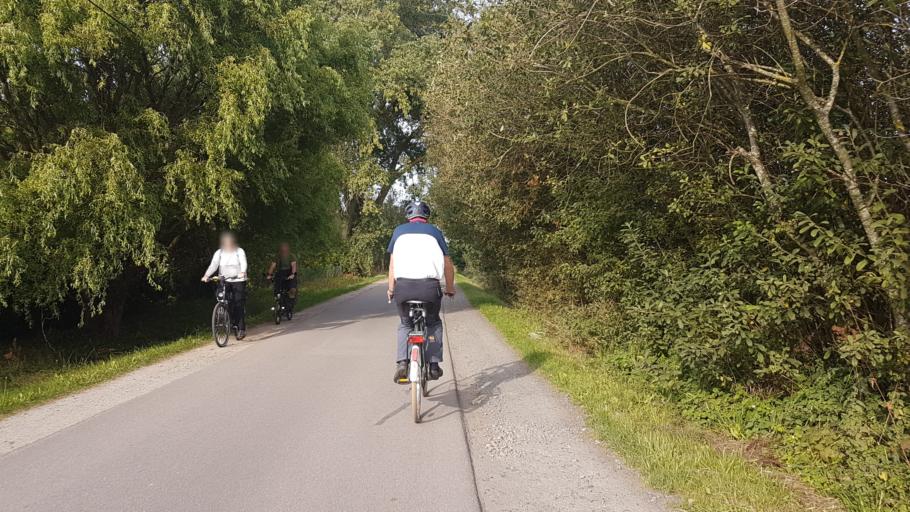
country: DE
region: Mecklenburg-Vorpommern
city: Hiddensee
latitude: 54.4645
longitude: 13.1394
